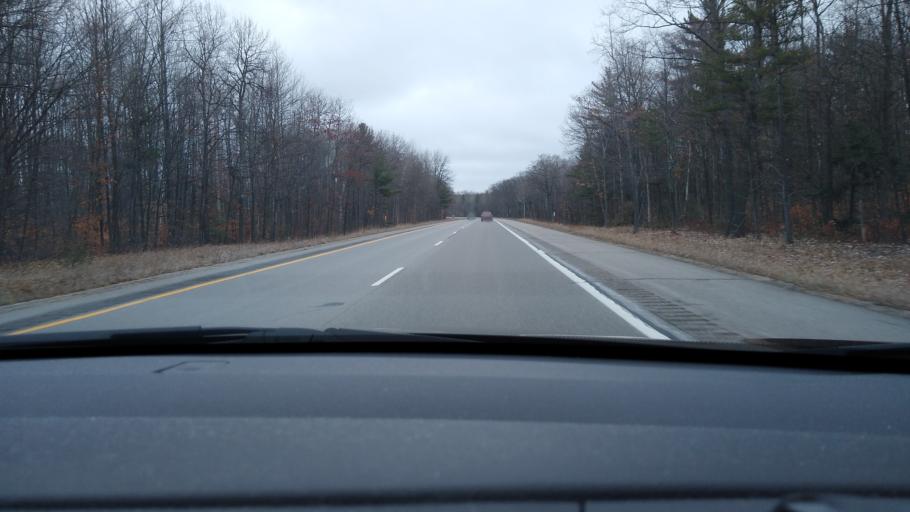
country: US
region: Michigan
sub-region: Otsego County
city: Gaylord
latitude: 44.9344
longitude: -84.6712
